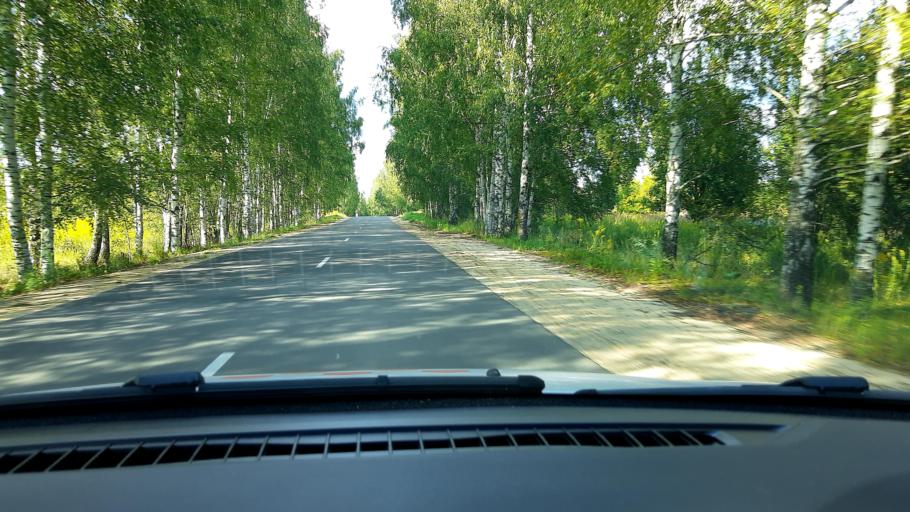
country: RU
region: Nizjnij Novgorod
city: Pamyat' Parizhskoy Kommuny
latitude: 56.2798
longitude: 44.4252
